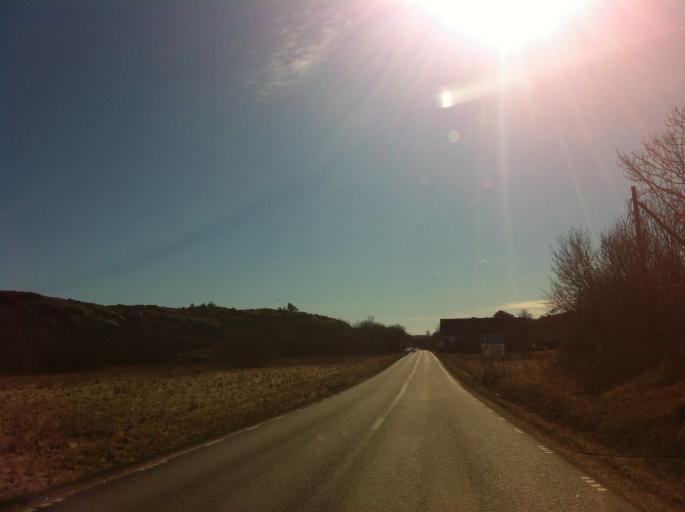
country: SE
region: Vaestra Goetaland
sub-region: Sotenas Kommun
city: Hunnebostrand
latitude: 58.4210
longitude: 11.2921
